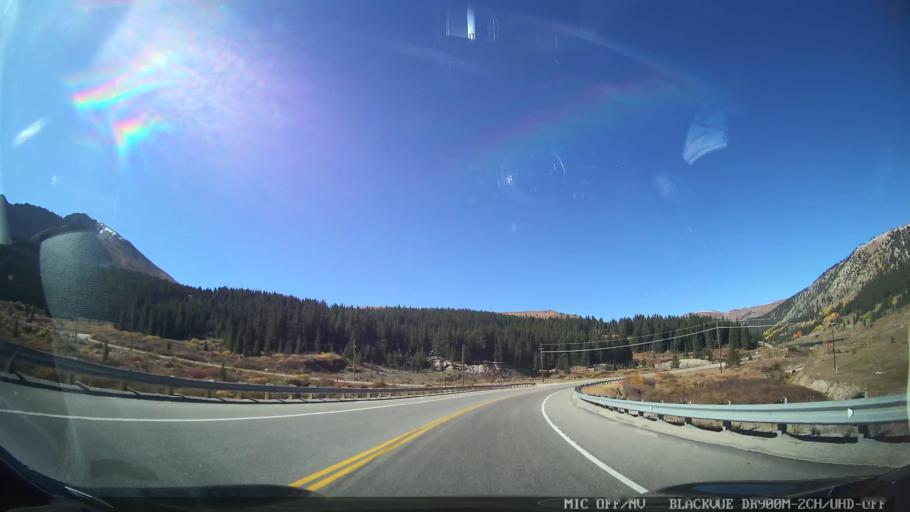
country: US
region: Colorado
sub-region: Lake County
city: Leadville
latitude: 39.3598
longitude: -106.1765
